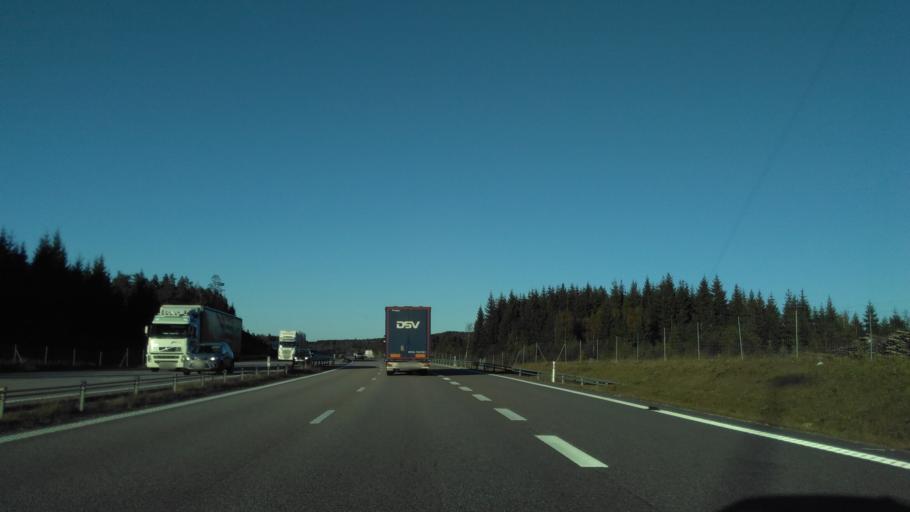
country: SE
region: Vaestra Goetaland
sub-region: Boras Kommun
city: Dalsjofors
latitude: 57.7606
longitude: 13.1069
